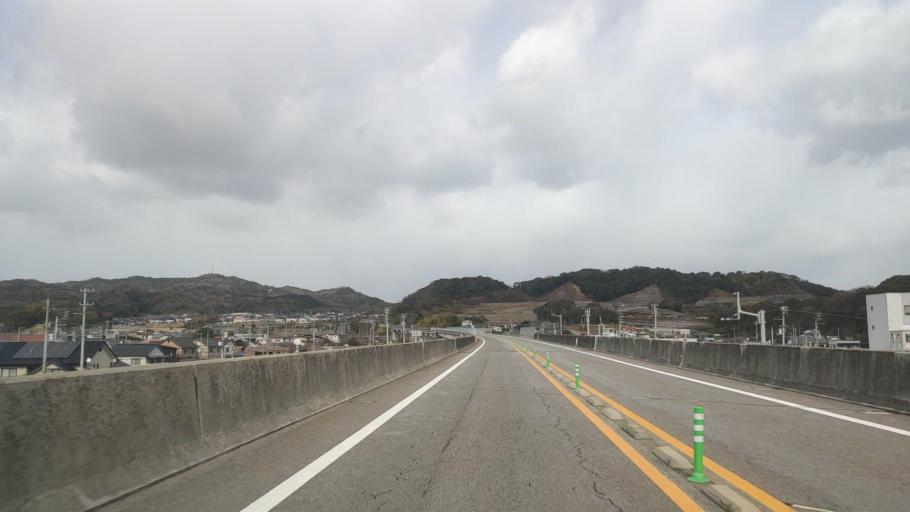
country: JP
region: Ehime
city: Hojo
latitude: 34.0597
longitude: 132.9718
